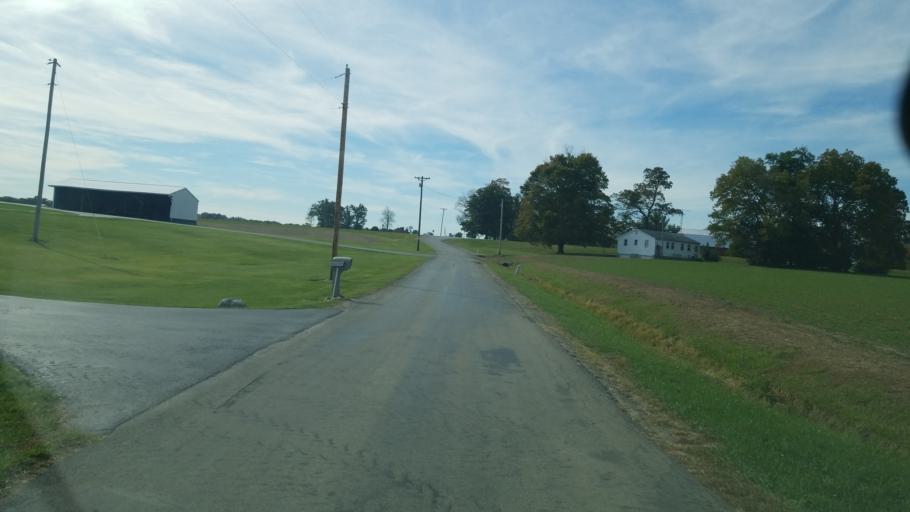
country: US
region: Ohio
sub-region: Highland County
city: Leesburg
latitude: 39.3294
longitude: -83.5616
